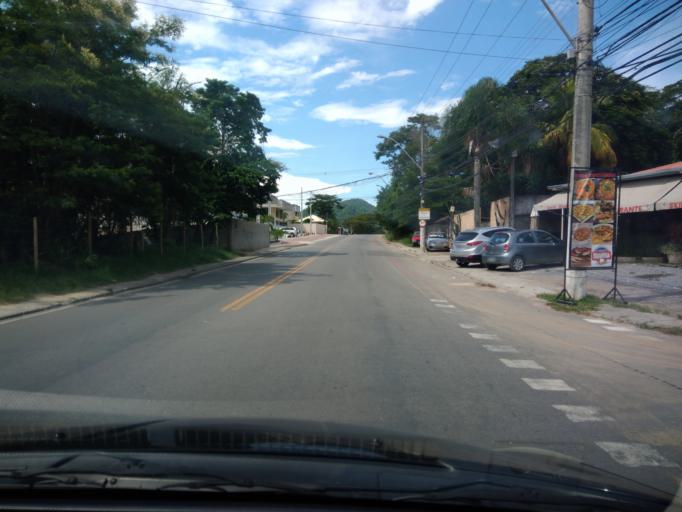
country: BR
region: Rio de Janeiro
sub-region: Niteroi
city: Niteroi
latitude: -22.9410
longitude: -43.0172
